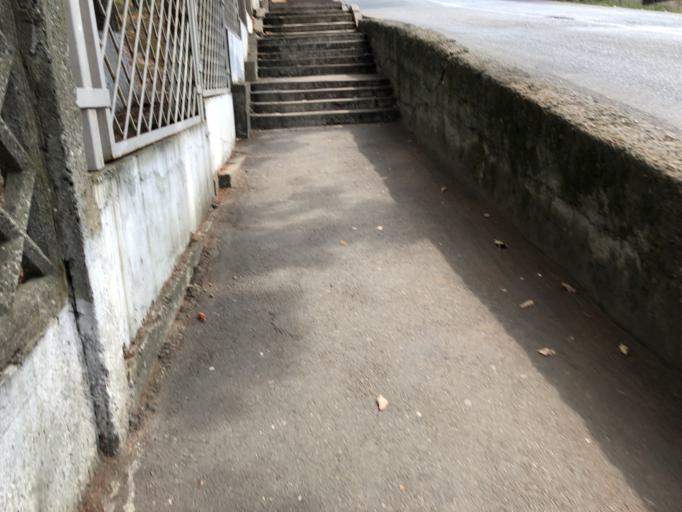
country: RU
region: Krasnodarskiy
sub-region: Sochi City
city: Sochi
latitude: 43.5916
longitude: 39.7361
